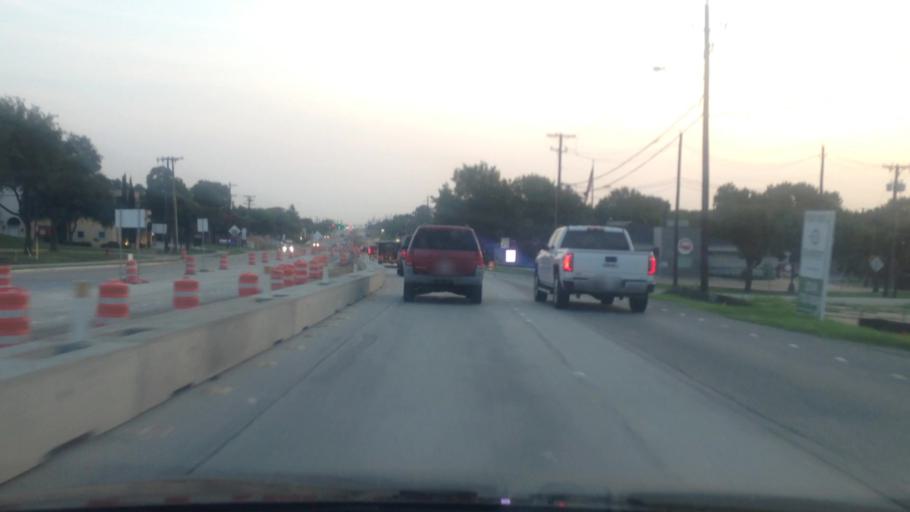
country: US
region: Texas
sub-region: Tarrant County
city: Colleyville
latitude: 32.8811
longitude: -97.1555
